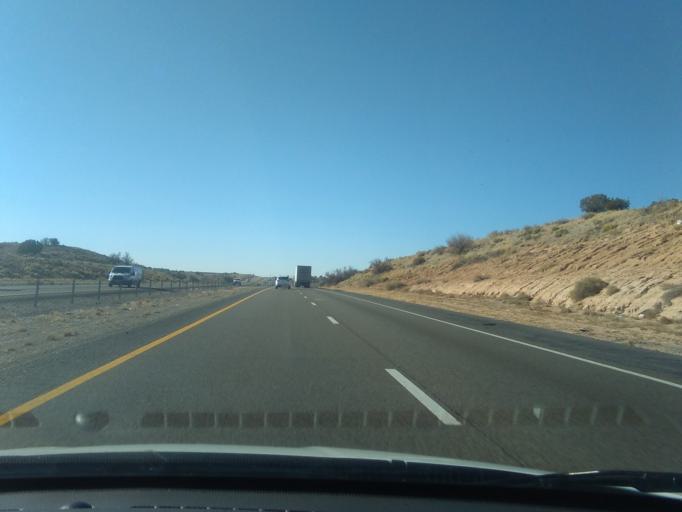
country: US
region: New Mexico
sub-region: Sandoval County
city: San Felipe Pueblo
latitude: 35.3673
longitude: -106.4836
